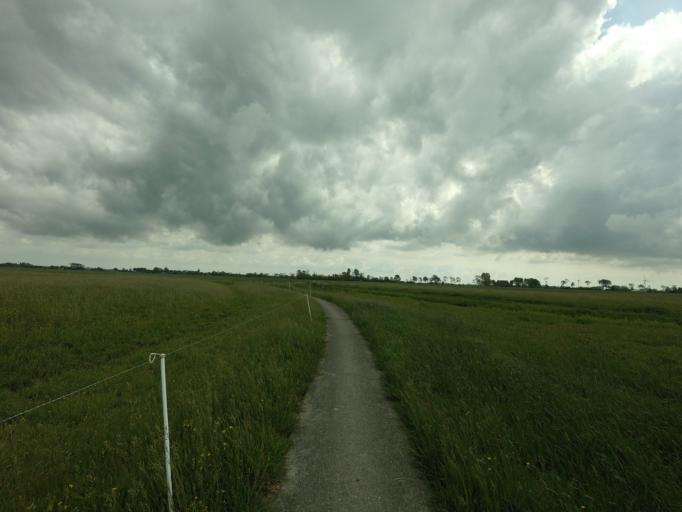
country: NL
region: Friesland
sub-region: Gemeente Littenseradiel
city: Wommels
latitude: 53.1091
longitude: 5.6042
